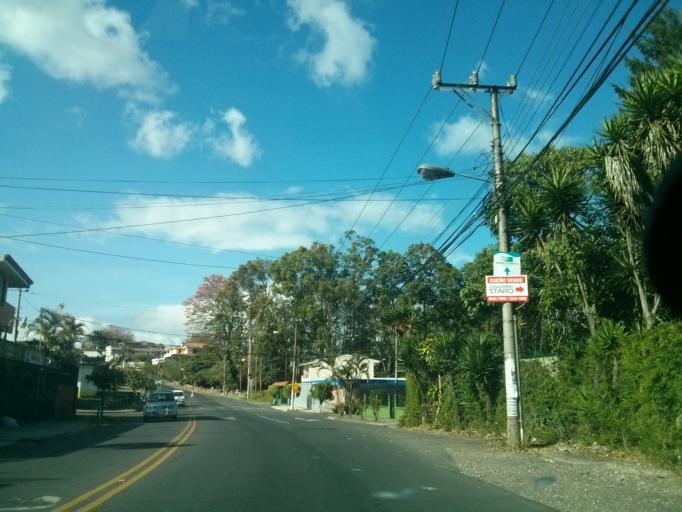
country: CR
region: San Jose
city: Curridabat
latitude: 9.9204
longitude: -84.0325
